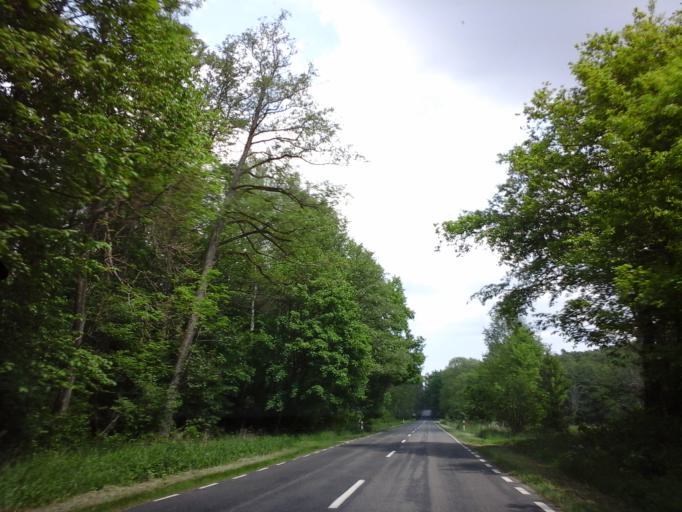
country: PL
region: West Pomeranian Voivodeship
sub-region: Powiat choszczenski
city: Drawno
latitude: 53.2372
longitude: 15.8117
